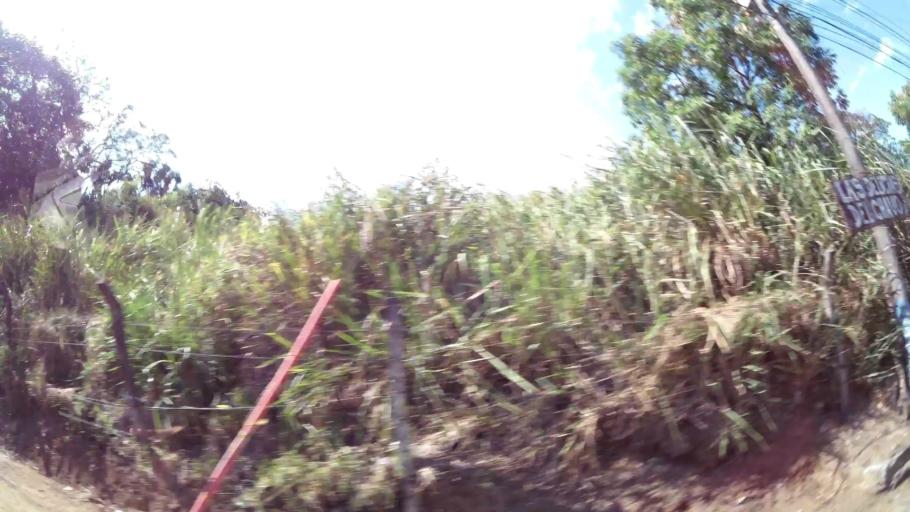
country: CO
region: Valle del Cauca
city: Cali
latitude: 3.4362
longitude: -76.5571
